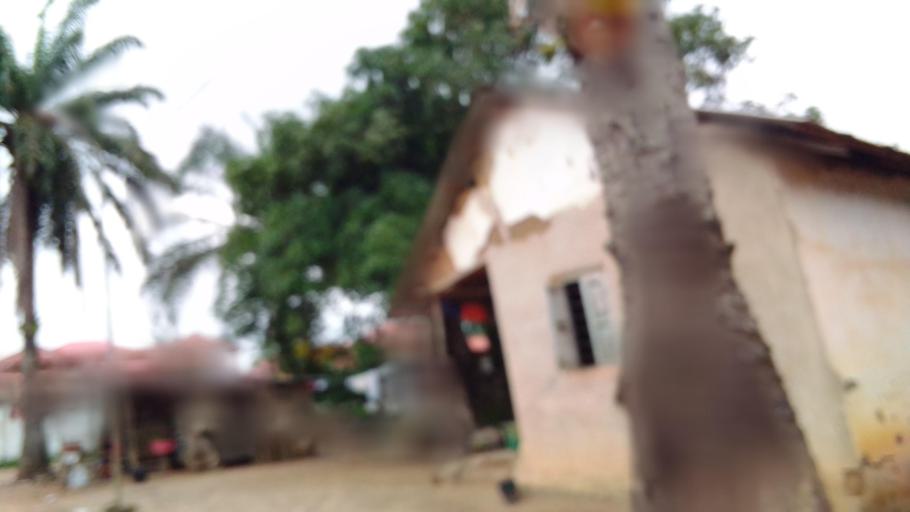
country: SL
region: Eastern Province
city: Kenema
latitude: 7.8551
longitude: -11.1974
